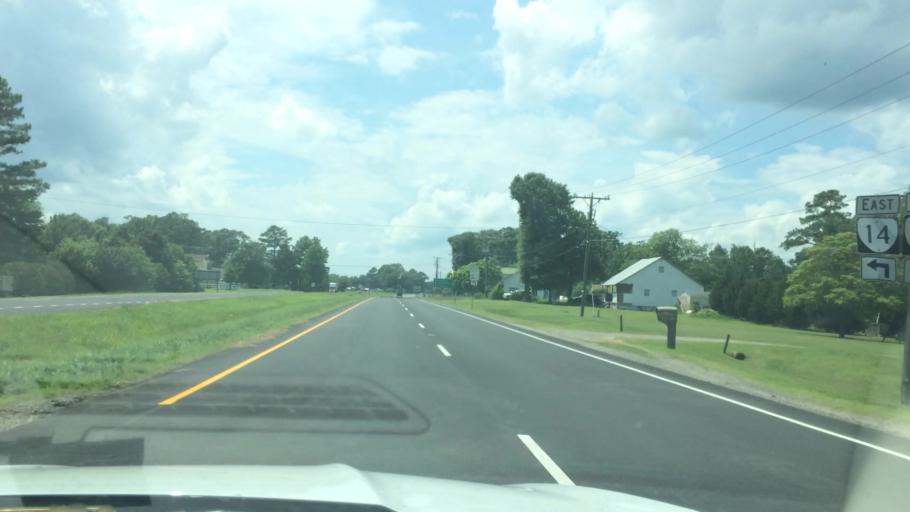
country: US
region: Virginia
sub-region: King William County
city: West Point
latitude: 37.5440
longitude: -76.7011
